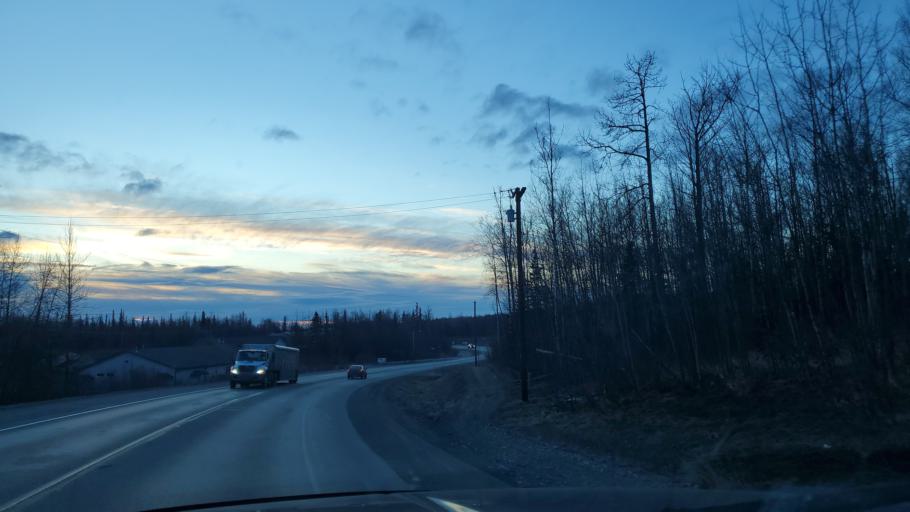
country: US
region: Alaska
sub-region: Matanuska-Susitna Borough
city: Wasilla
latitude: 61.5953
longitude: -149.4317
